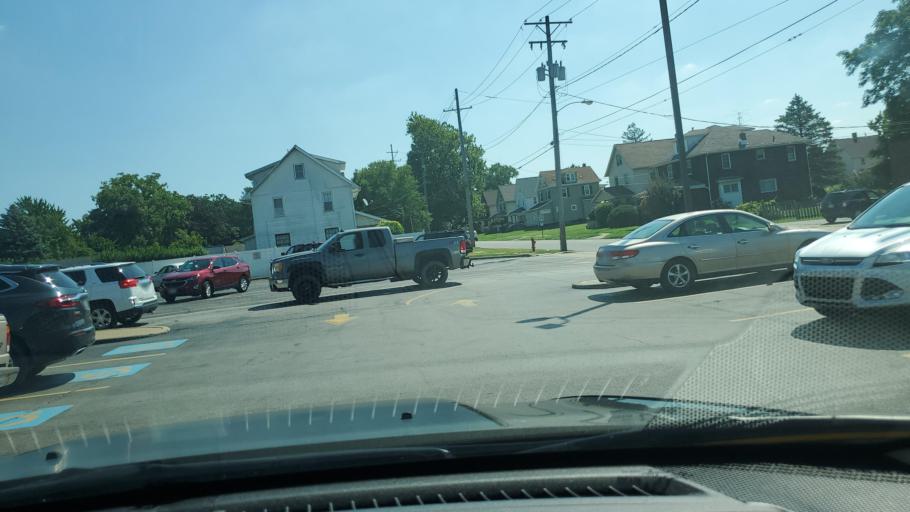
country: US
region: Ohio
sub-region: Trumbull County
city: Girard
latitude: 41.1505
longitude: -80.6995
